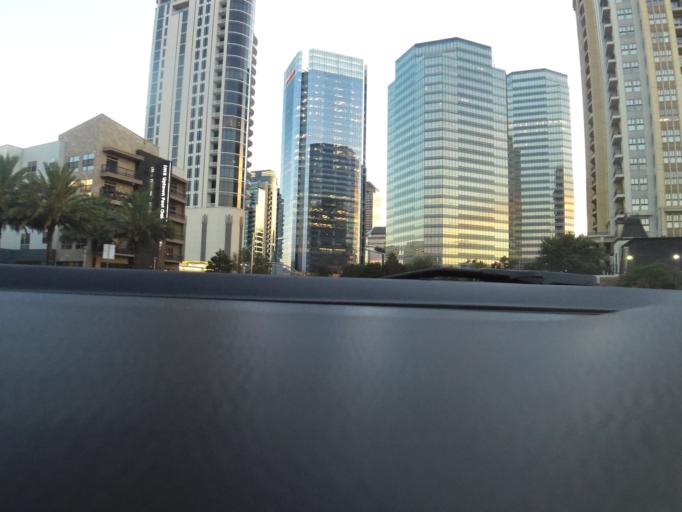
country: US
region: Texas
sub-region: Harris County
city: Hunters Creek Village
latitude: 29.7535
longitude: -95.4581
